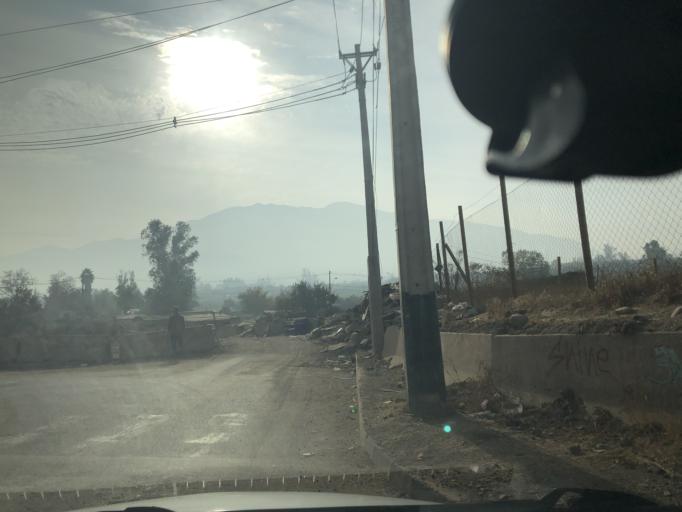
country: CL
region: Santiago Metropolitan
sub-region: Provincia de Cordillera
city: Puente Alto
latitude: -33.5854
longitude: -70.5490
